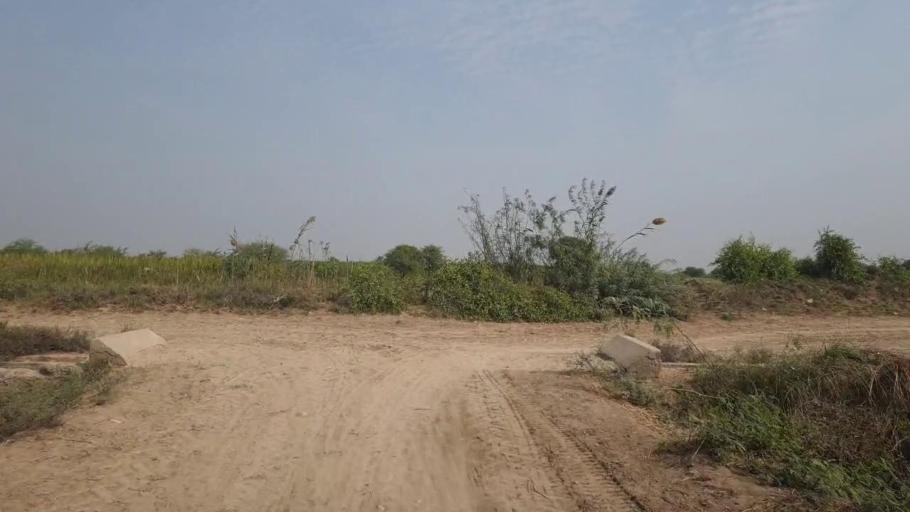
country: PK
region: Sindh
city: Tando Muhammad Khan
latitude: 25.1624
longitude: 68.4712
